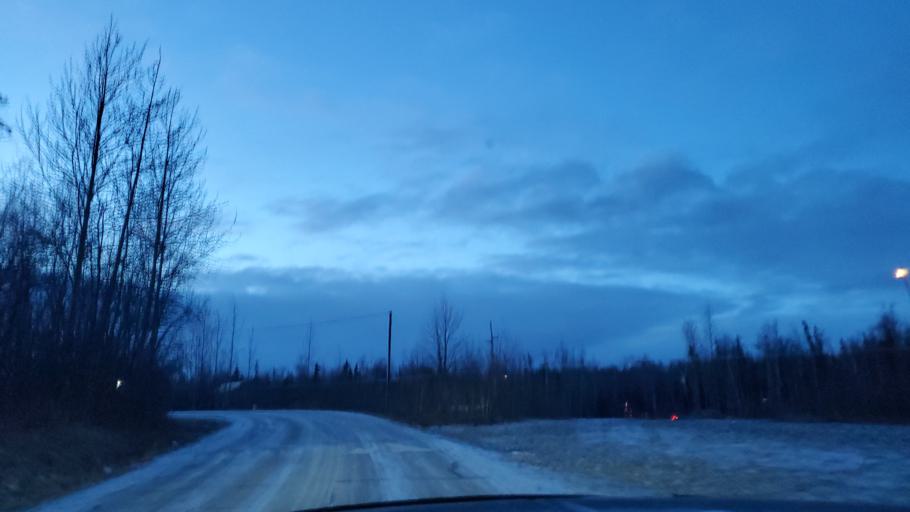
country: US
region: Alaska
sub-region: Matanuska-Susitna Borough
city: Lakes
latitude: 61.5977
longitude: -149.3612
